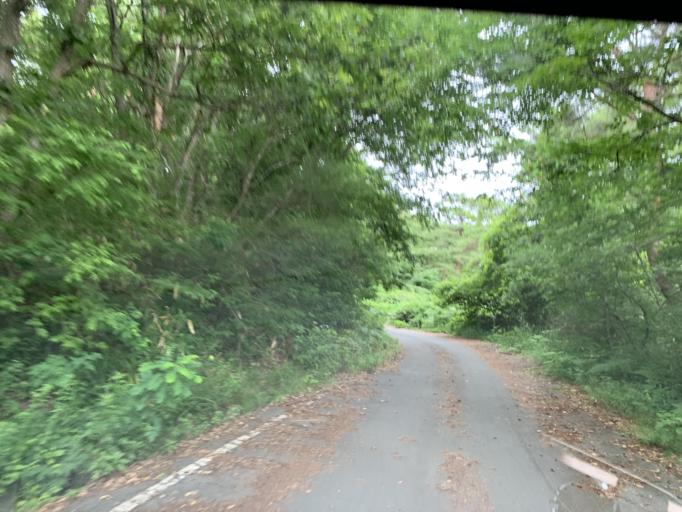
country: JP
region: Iwate
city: Ichinoseki
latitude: 38.8286
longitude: 141.2132
